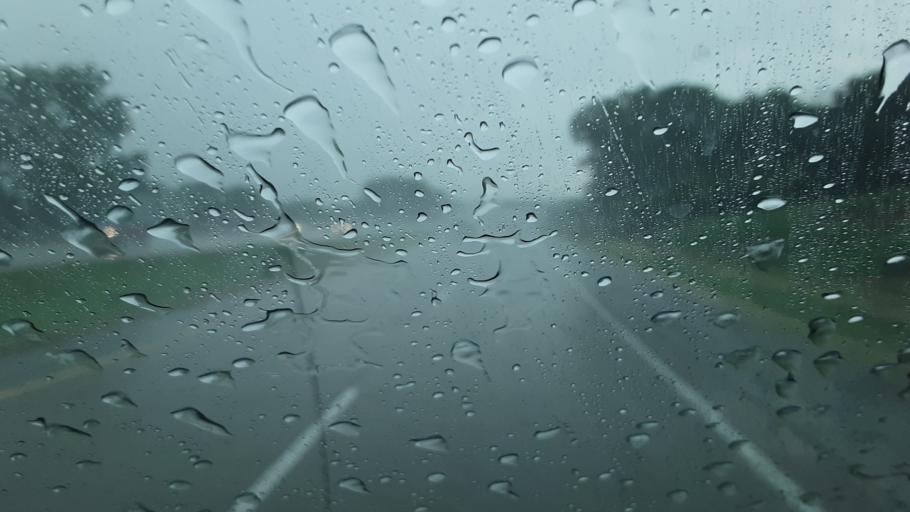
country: US
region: Iowa
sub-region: Pottawattamie County
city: Council Bluffs
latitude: 41.2578
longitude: -95.8054
